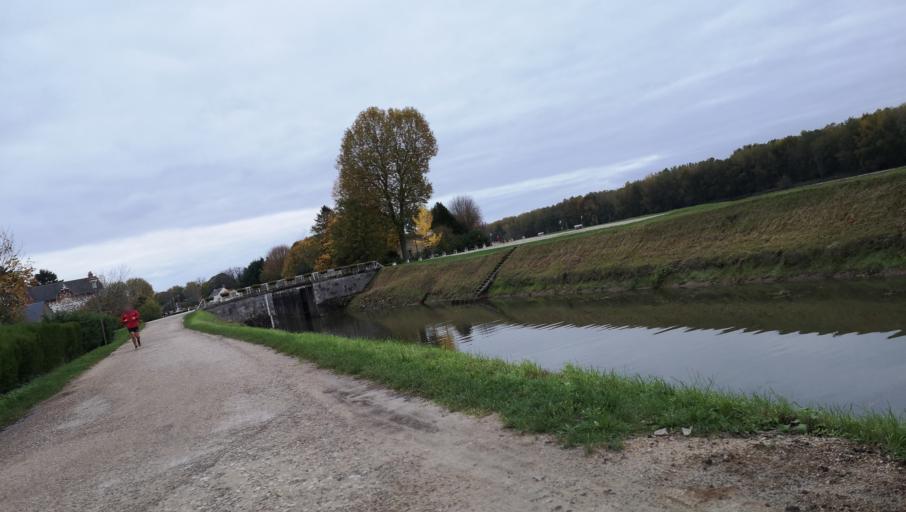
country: FR
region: Centre
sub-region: Departement du Loiret
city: Saint-Jean-de-Braye
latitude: 47.9012
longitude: 1.9836
